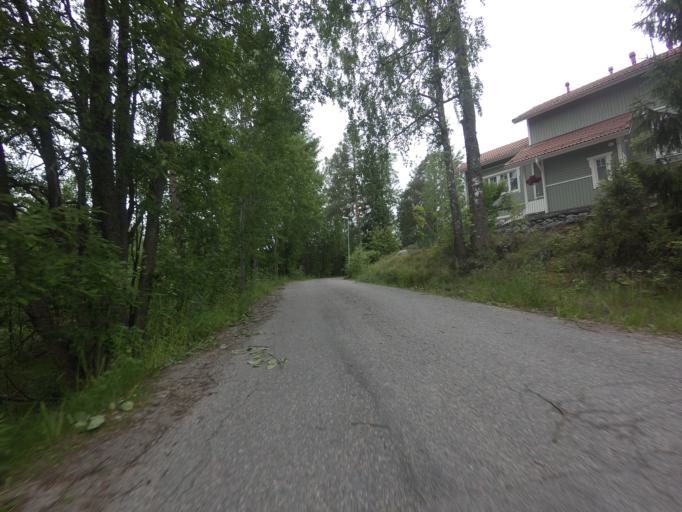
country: FI
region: Uusimaa
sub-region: Helsinki
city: Kauniainen
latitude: 60.1883
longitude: 24.7297
